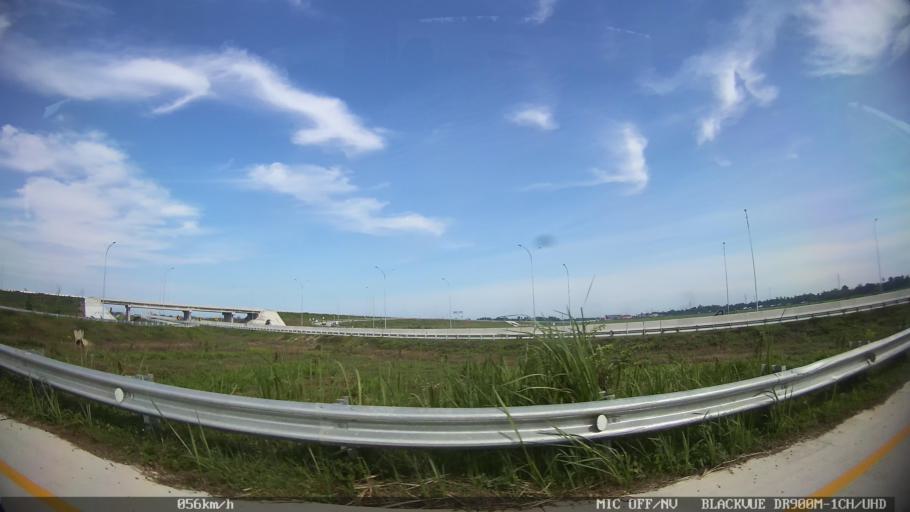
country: ID
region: North Sumatra
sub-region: Kabupaten Langkat
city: Stabat
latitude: 3.7132
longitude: 98.4972
